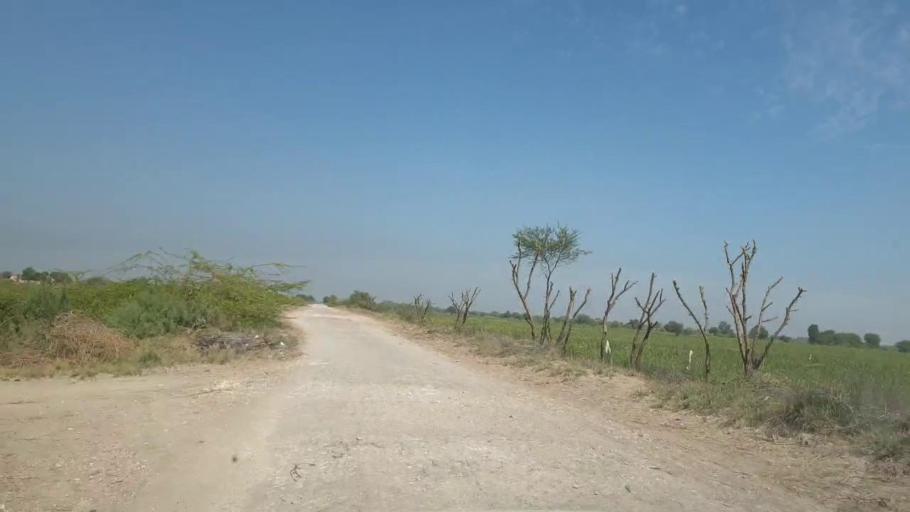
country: PK
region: Sindh
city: Mirpur Khas
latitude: 25.5911
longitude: 69.2010
